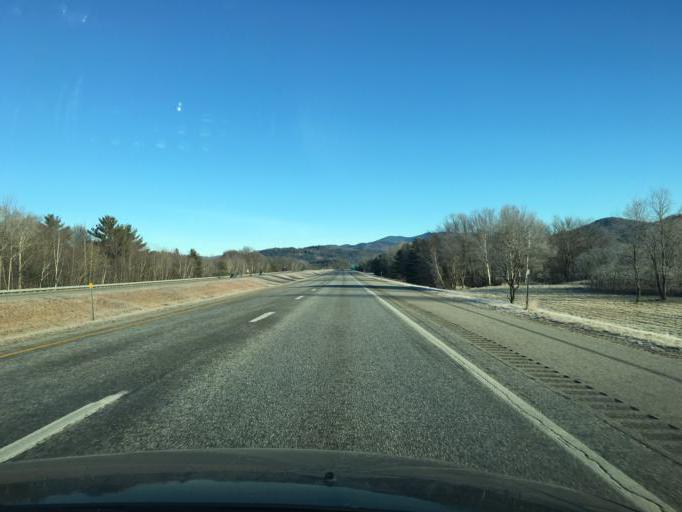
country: US
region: New Hampshire
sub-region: Grafton County
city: Thornton
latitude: 43.8268
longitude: -71.6569
